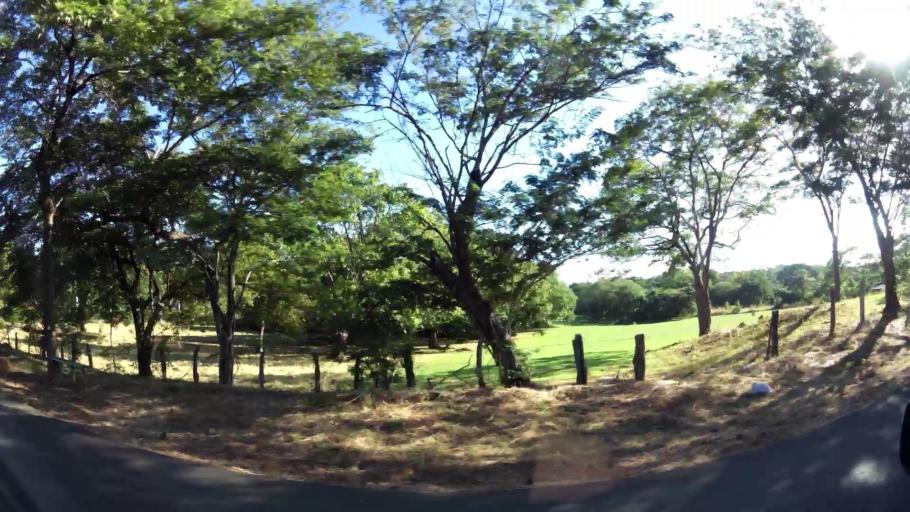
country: CR
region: Guanacaste
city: Sardinal
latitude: 10.4963
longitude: -85.6364
